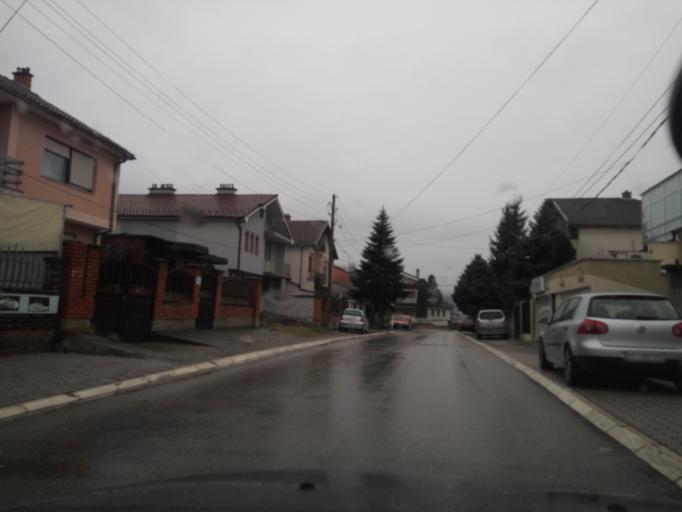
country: XK
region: Gjakova
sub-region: Komuna e Gjakoves
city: Gjakove
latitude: 42.3694
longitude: 20.4408
